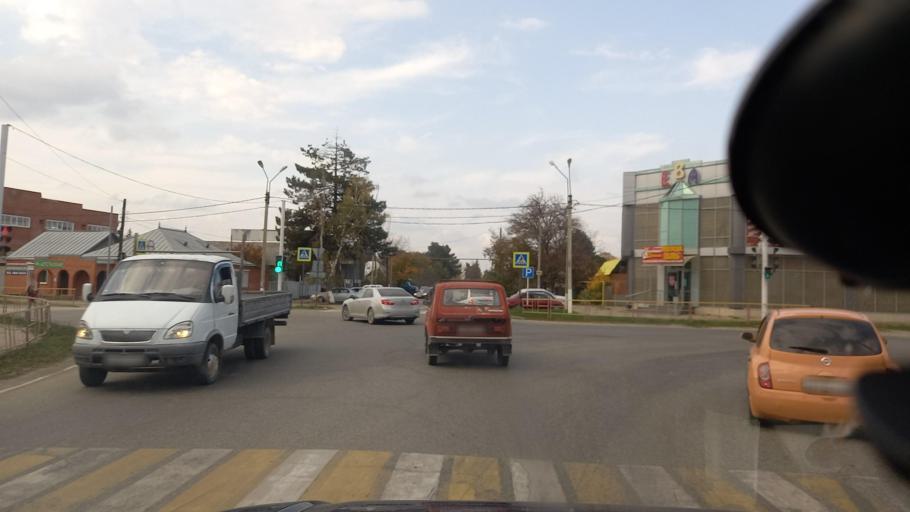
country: RU
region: Krasnodarskiy
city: Mostovskoy
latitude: 44.4084
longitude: 40.8036
